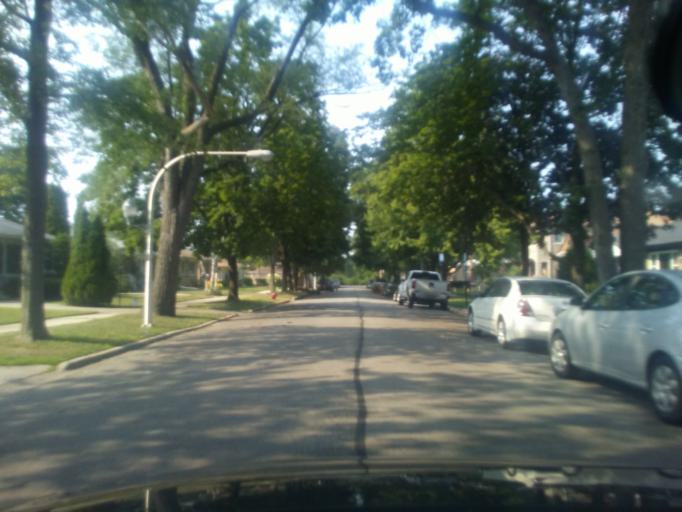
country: US
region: Illinois
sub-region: Cook County
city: Lincolnwood
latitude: 41.9959
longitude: -87.7326
